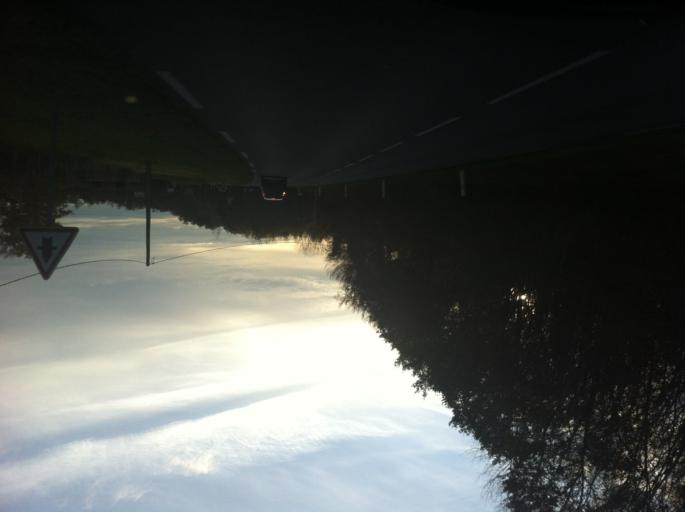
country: FR
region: Aquitaine
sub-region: Departement de la Dordogne
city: Tocane-Saint-Apre
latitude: 45.2527
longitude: 0.5154
